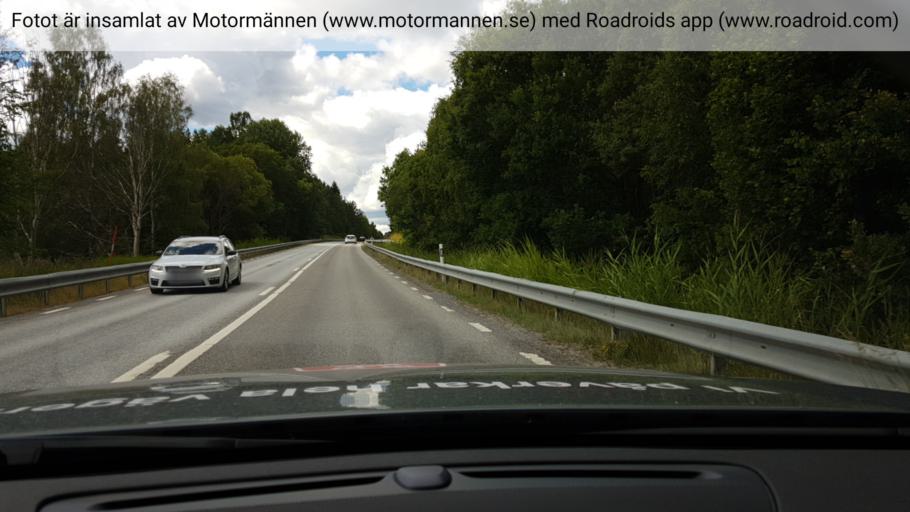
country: SE
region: Stockholm
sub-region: Vaxholms Kommun
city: Resaro
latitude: 59.4235
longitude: 18.2861
